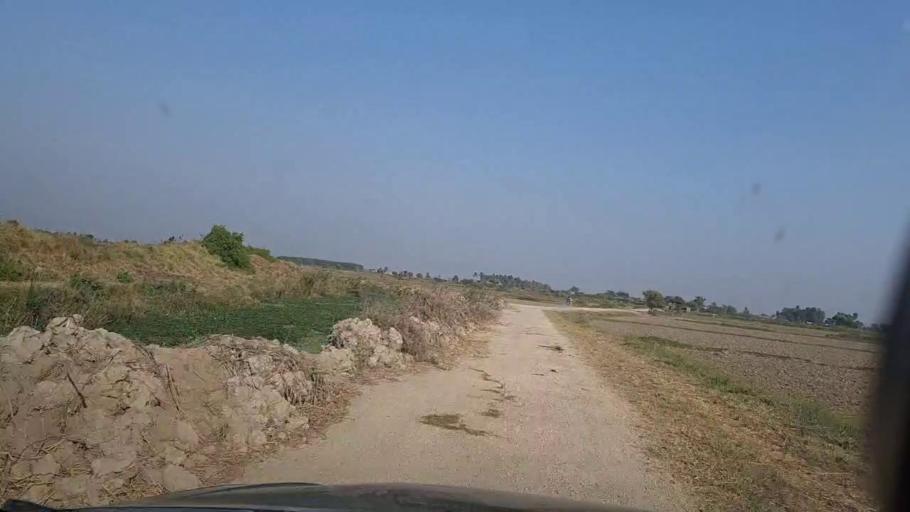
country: PK
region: Sindh
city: Thatta
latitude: 24.5862
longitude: 67.8811
